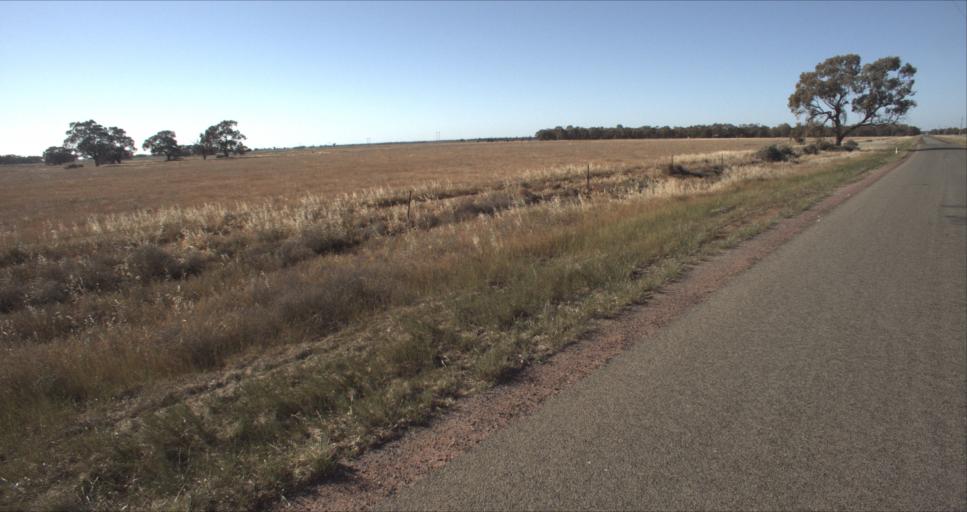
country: AU
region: New South Wales
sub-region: Leeton
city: Leeton
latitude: -34.5557
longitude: 146.2664
